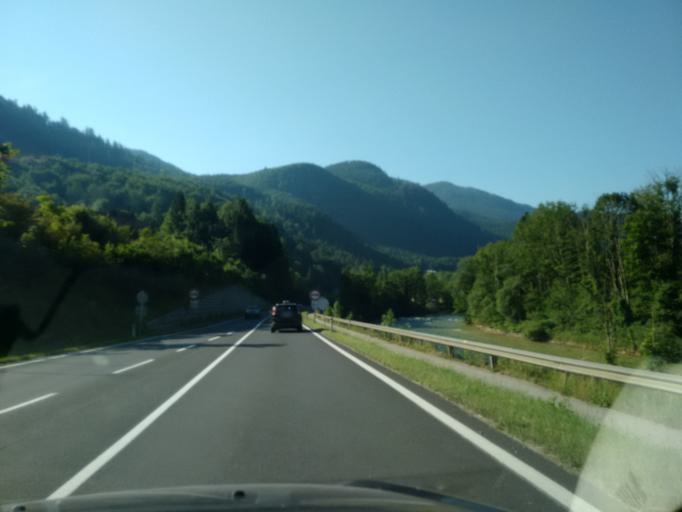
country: AT
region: Upper Austria
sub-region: Politischer Bezirk Gmunden
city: Bad Ischl
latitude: 47.6887
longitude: 13.6252
